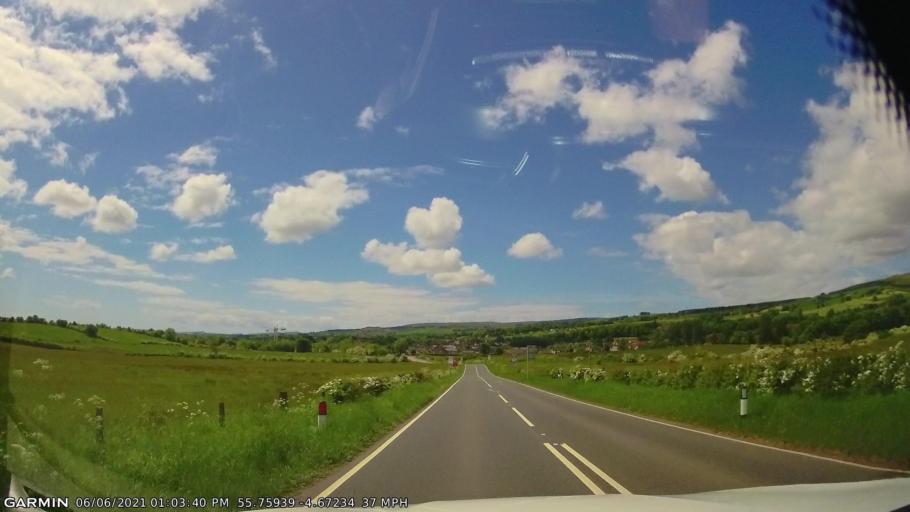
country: GB
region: Scotland
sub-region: North Ayrshire
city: Kilbirnie
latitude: 55.7593
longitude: -4.6728
